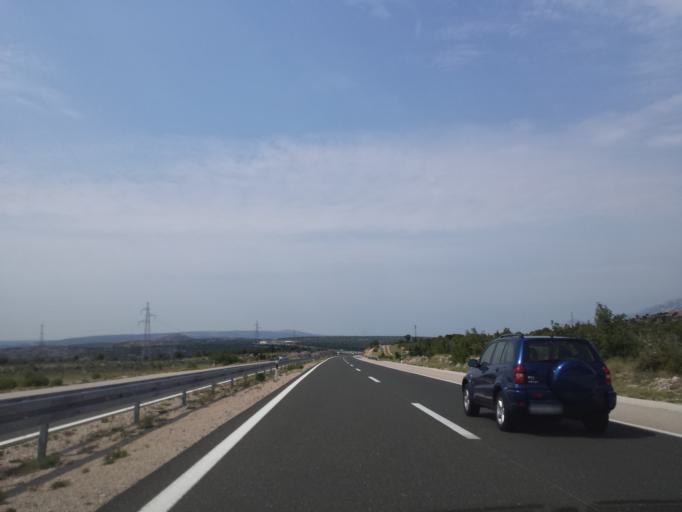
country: HR
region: Zadarska
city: Pridraga
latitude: 44.2389
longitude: 15.5955
